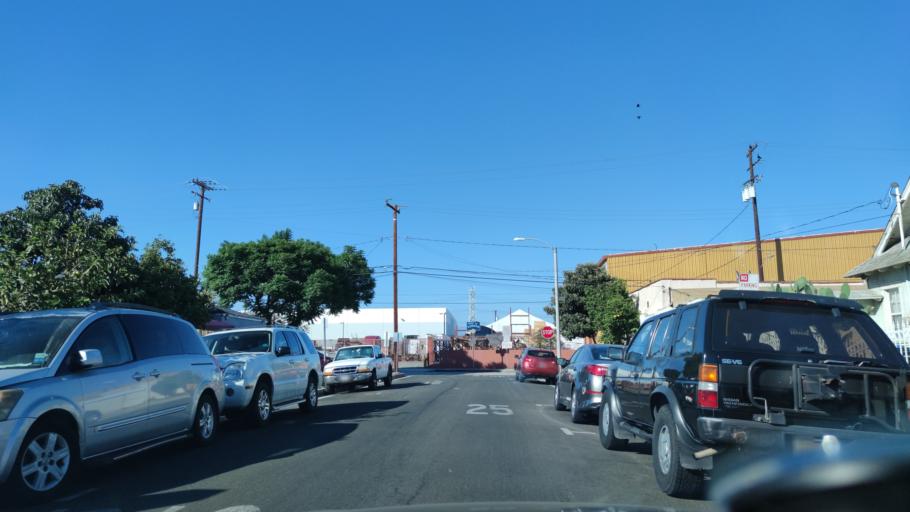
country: US
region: California
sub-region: Los Angeles County
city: Maywood
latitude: 33.9905
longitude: -118.1800
